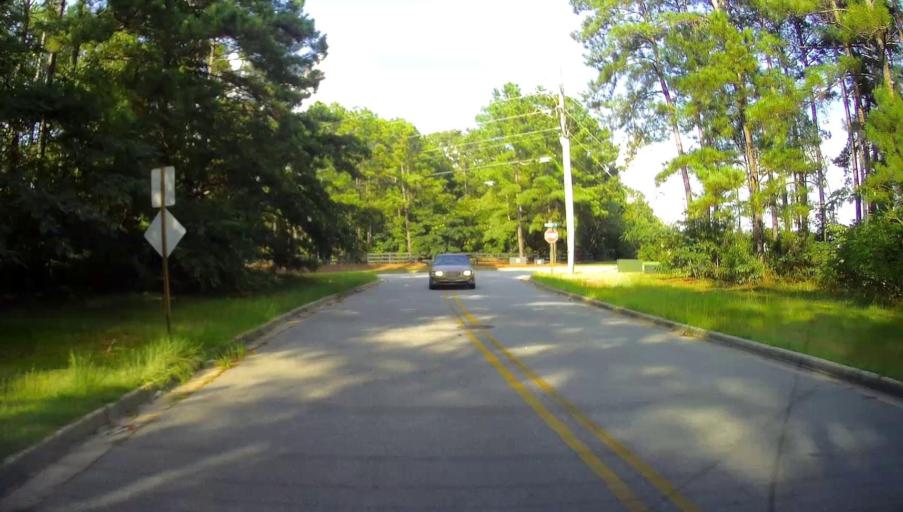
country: US
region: Georgia
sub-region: Houston County
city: Warner Robins
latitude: 32.5873
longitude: -83.6374
